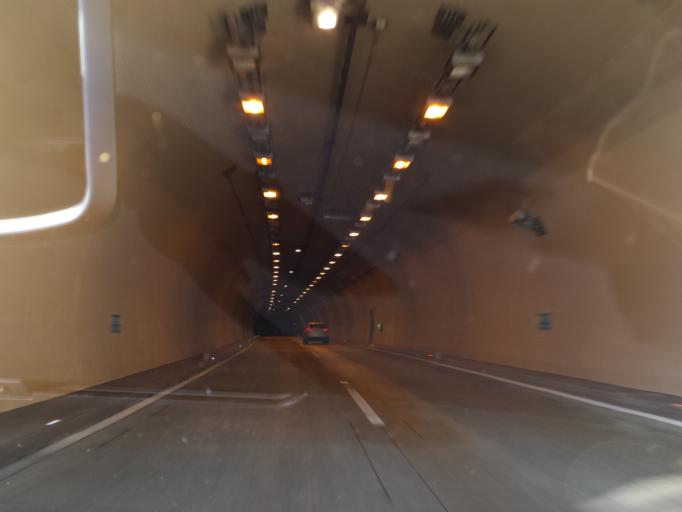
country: AT
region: Styria
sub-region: Politischer Bezirk Bruck-Muerzzuschlag
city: Pernegg an der Mur
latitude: 47.3796
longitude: 15.3048
